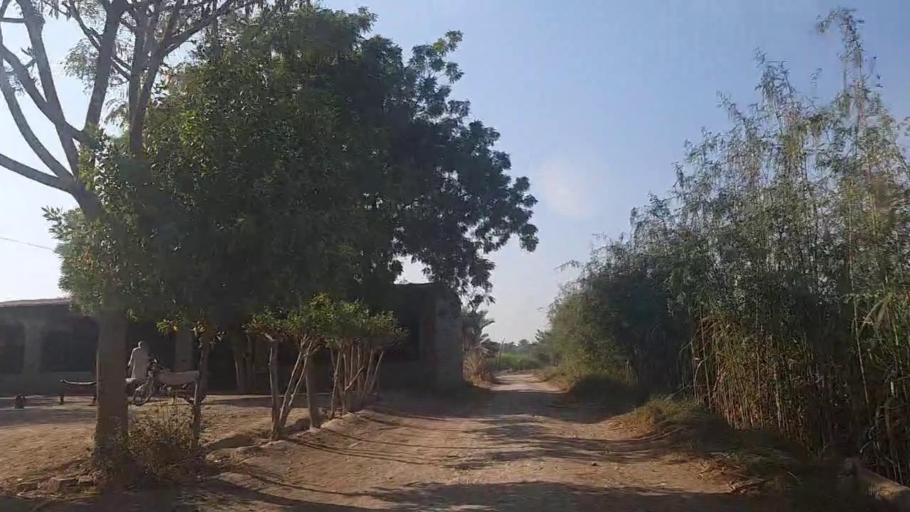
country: PK
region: Sindh
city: Gambat
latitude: 27.3665
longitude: 68.4757
